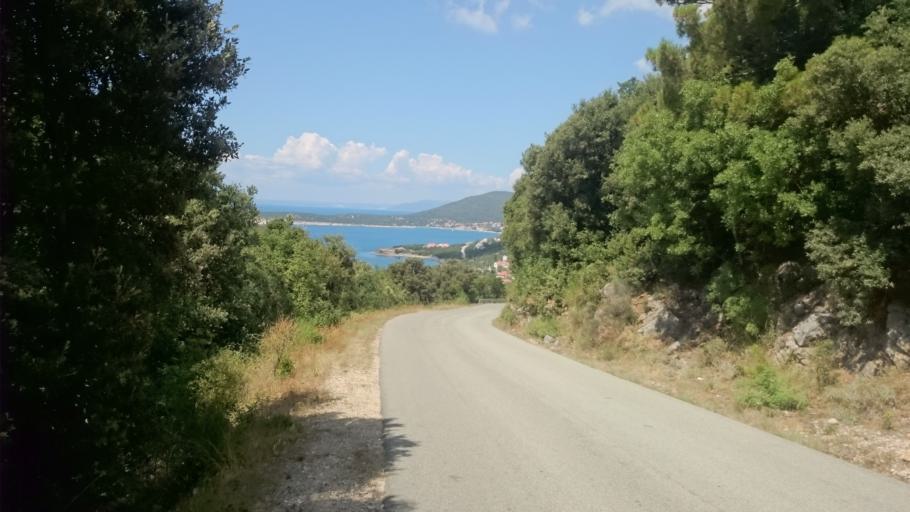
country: HR
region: Primorsko-Goranska
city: Cres
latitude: 44.7973
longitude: 14.3760
